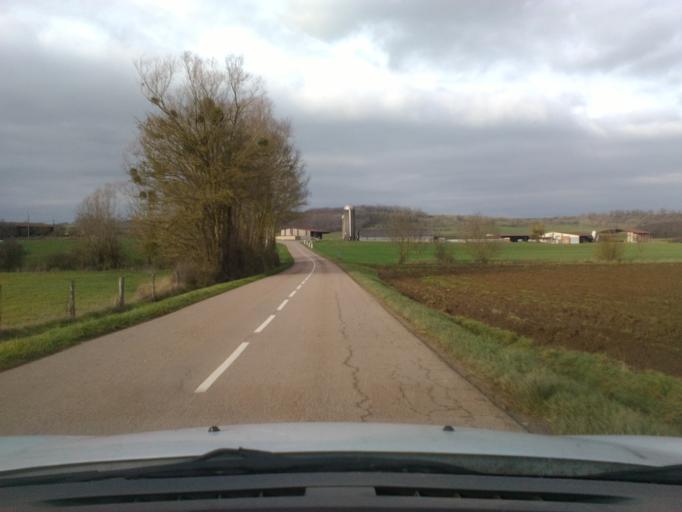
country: FR
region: Lorraine
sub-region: Departement des Vosges
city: Mirecourt
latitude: 48.3340
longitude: 6.0264
